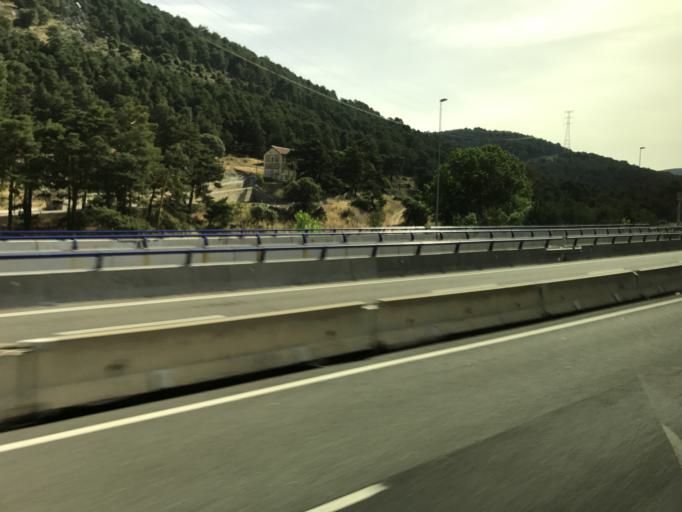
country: ES
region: Castille and Leon
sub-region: Provincia de Avila
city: Peguerinos
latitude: 40.7142
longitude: -4.1833
